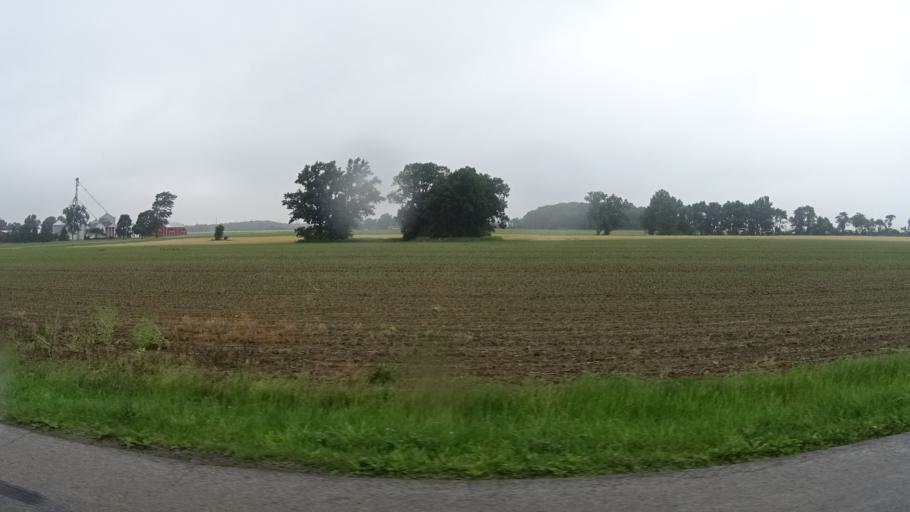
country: US
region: Ohio
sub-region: Huron County
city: Bellevue
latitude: 41.2990
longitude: -82.8403
